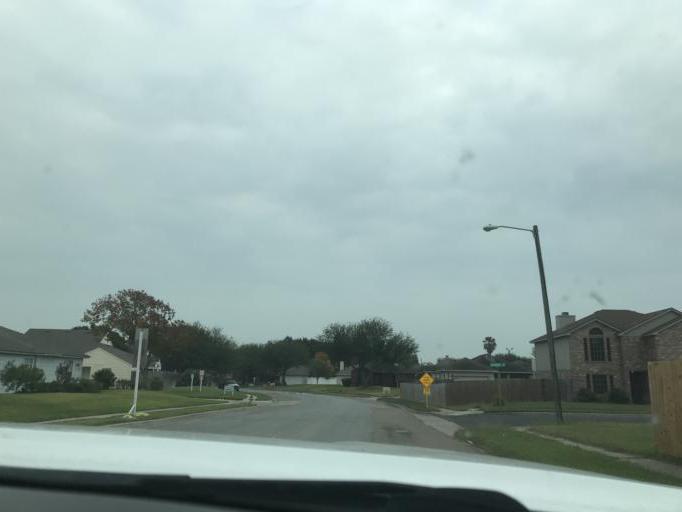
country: US
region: Texas
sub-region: Nueces County
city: Corpus Christi
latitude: 27.6692
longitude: -97.3560
